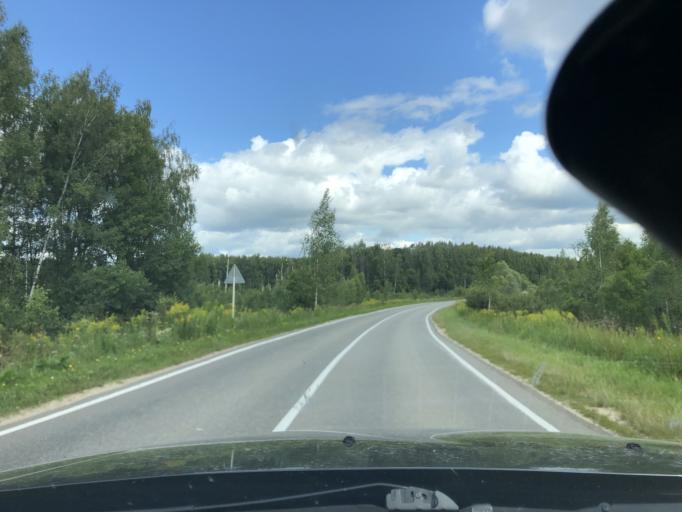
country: RU
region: Tula
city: Yasnogorsk
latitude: 54.4218
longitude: 37.6911
